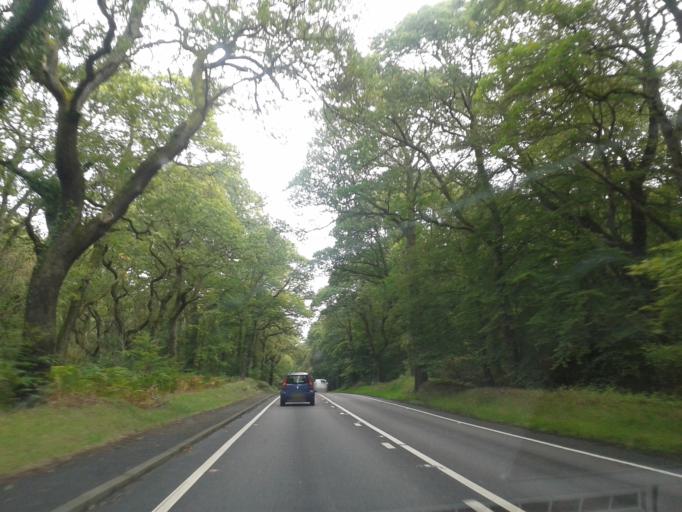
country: GB
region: Scotland
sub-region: Moray
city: Elgin
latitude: 57.6475
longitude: -3.3577
